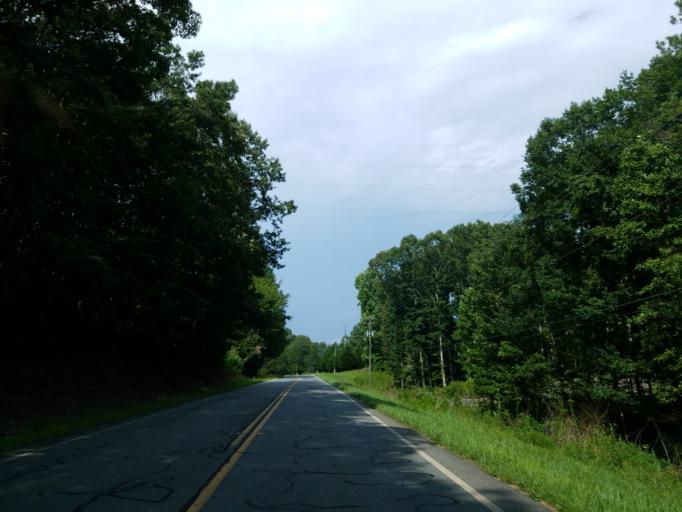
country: US
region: Georgia
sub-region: Gilmer County
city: Ellijay
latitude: 34.6213
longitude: -84.5801
